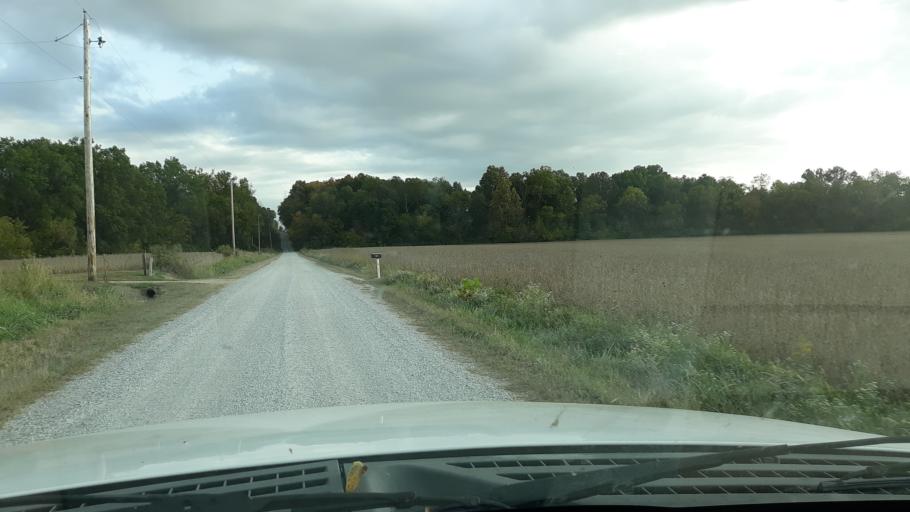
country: US
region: Illinois
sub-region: Saline County
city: Eldorado
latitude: 37.8333
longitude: -88.5026
